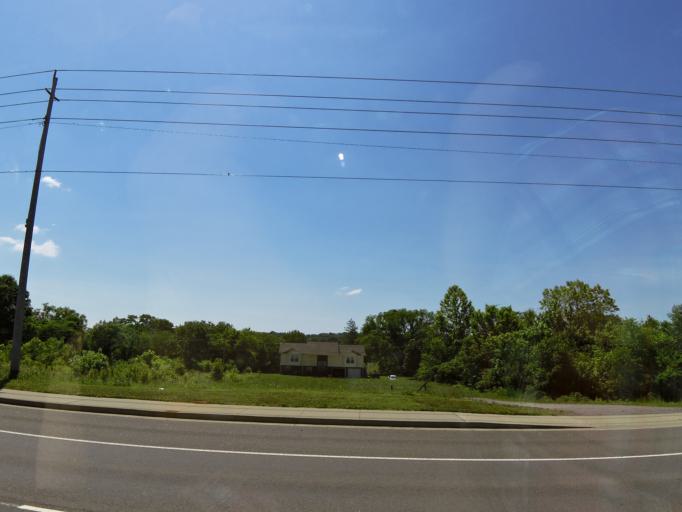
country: US
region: Tennessee
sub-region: Sevier County
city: Sevierville
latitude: 35.9133
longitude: -83.5811
